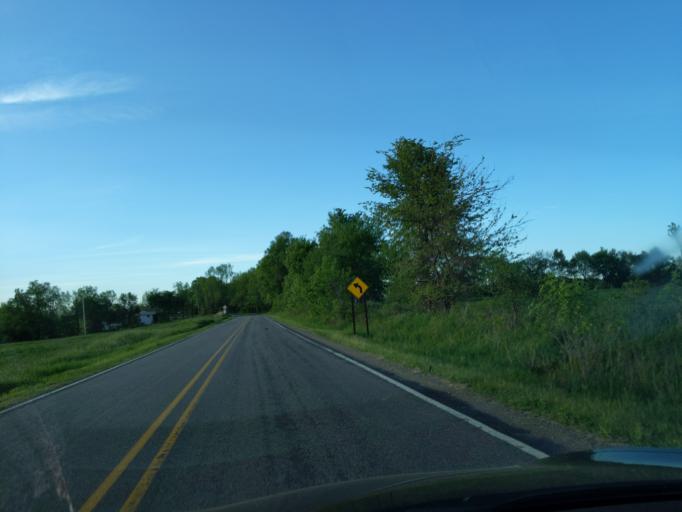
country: US
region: Michigan
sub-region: Ingham County
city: Leslie
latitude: 42.4446
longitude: -84.3134
